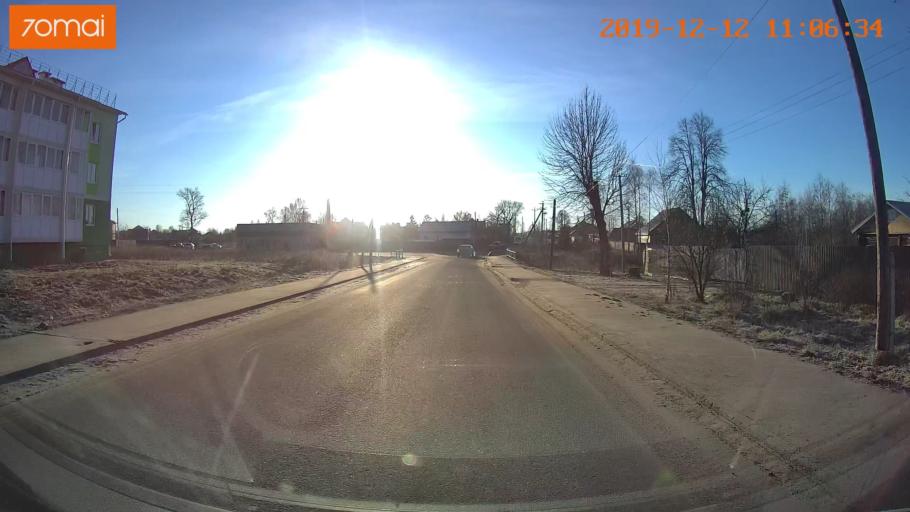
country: RU
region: Ivanovo
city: Kokhma
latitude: 56.9430
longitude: 41.0885
